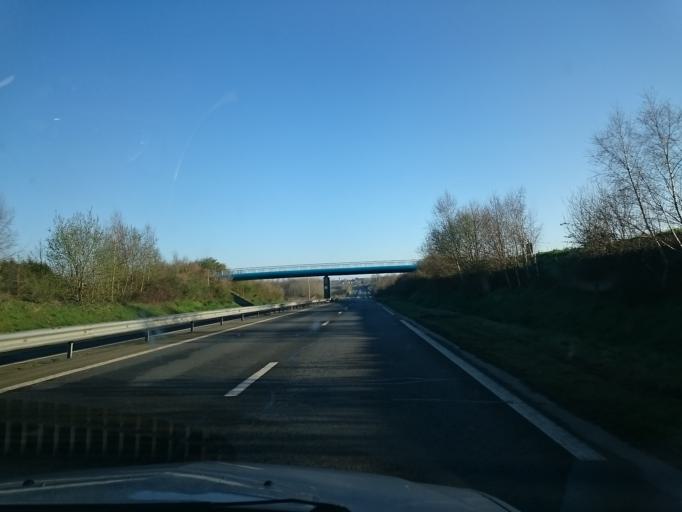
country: FR
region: Brittany
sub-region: Departement d'Ille-et-Vilaine
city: Saint-Armel
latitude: 48.0231
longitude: -1.6010
